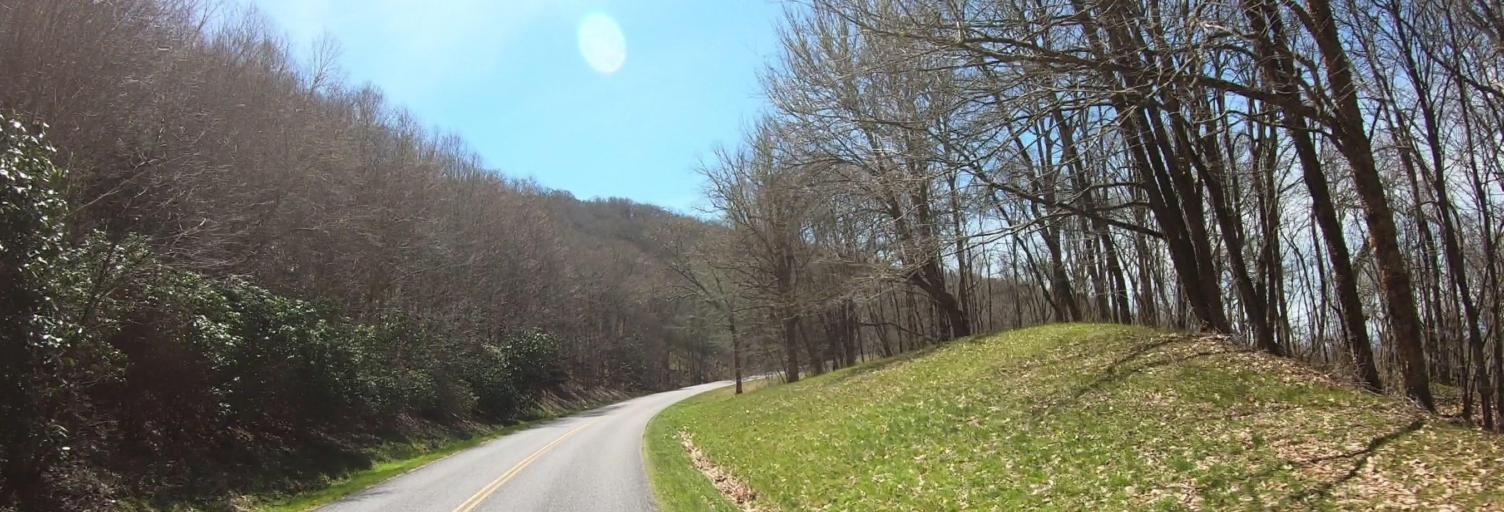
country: US
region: North Carolina
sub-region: Haywood County
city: Maggie Valley
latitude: 35.5123
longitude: -83.1887
